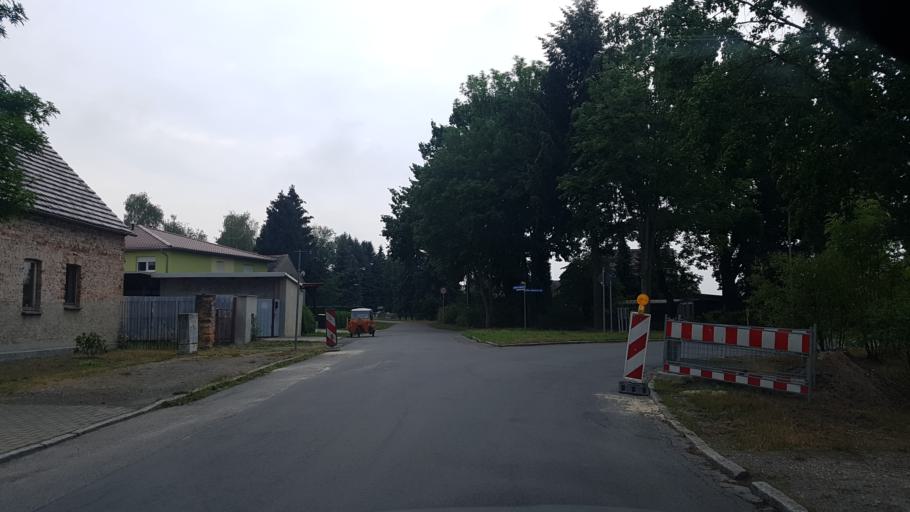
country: DE
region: Saxony
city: Bernsdorf
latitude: 51.3731
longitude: 14.0774
